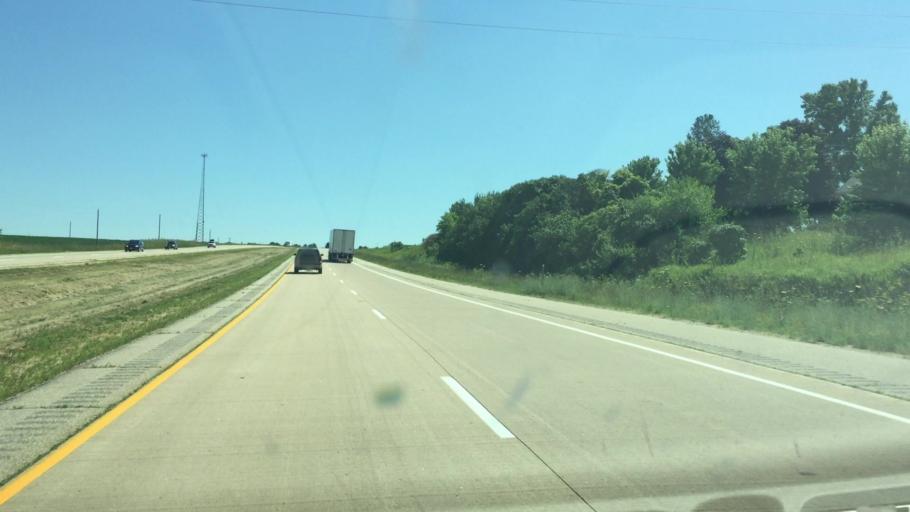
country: US
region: Wisconsin
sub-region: Iowa County
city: Mineral Point
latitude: 42.7714
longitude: -90.3132
